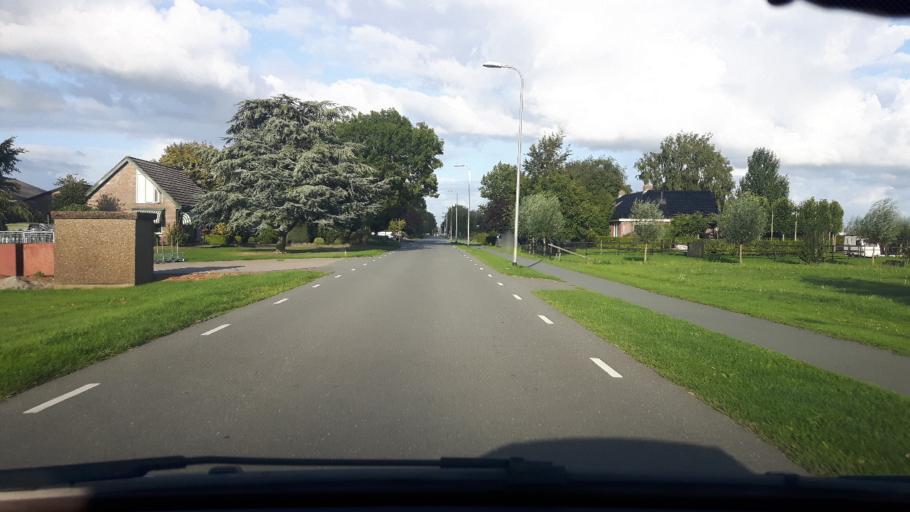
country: NL
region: Overijssel
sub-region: Gemeente Kampen
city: Kampen
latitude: 52.5766
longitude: 5.9574
